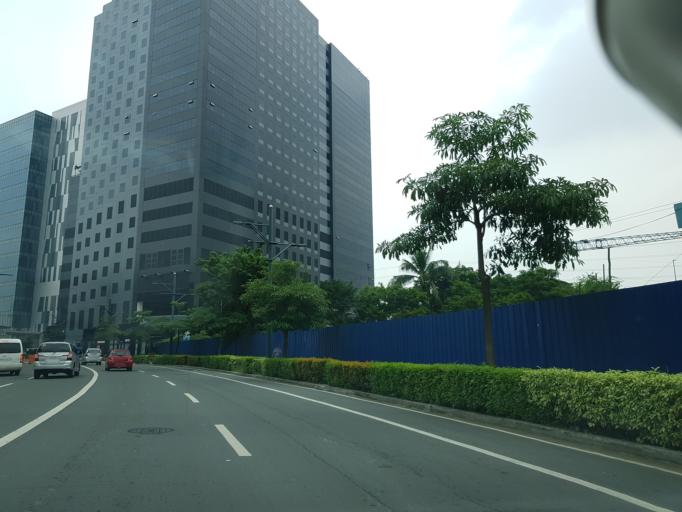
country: PH
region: Metro Manila
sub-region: Makati City
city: Makati City
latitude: 14.5363
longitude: 121.0424
